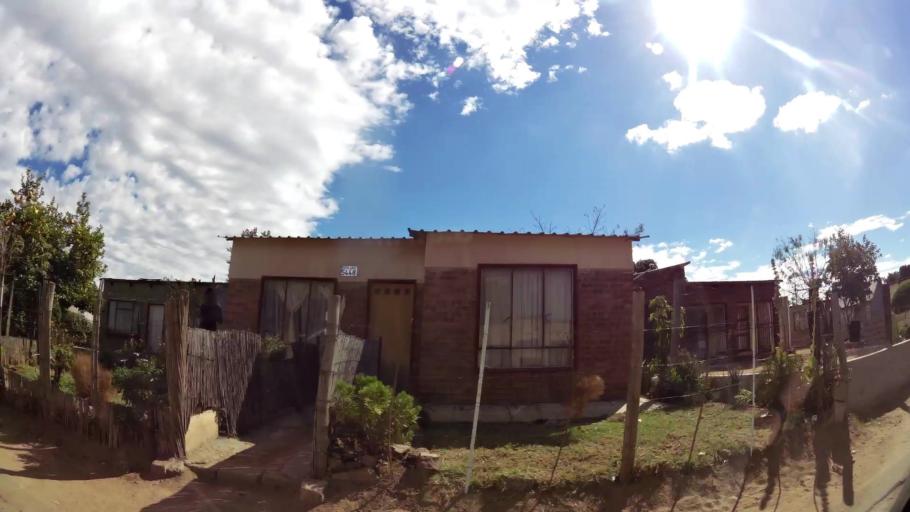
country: ZA
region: Limpopo
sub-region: Waterberg District Municipality
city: Bela-Bela
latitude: -24.8808
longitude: 28.3180
